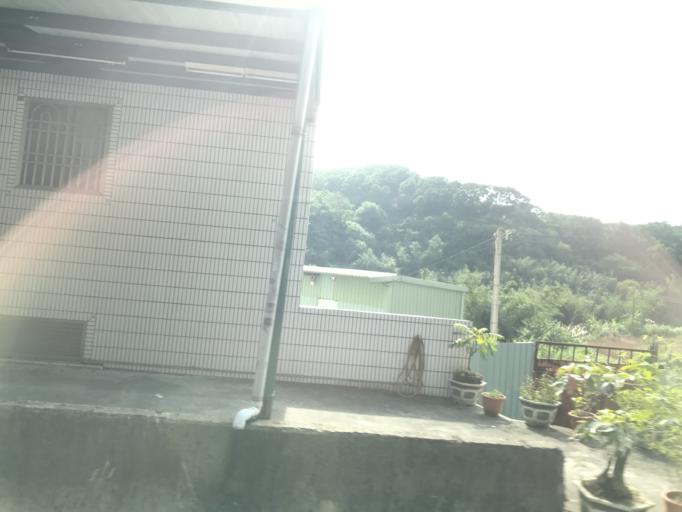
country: TW
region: Taiwan
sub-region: Hsinchu
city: Hsinchu
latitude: 24.7795
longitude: 120.9357
